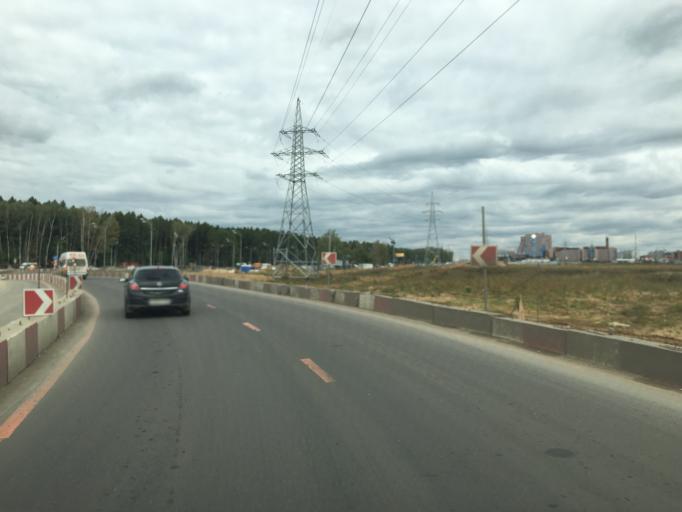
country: RU
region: Moskovskaya
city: Kommunarka
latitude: 55.5725
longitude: 37.4580
